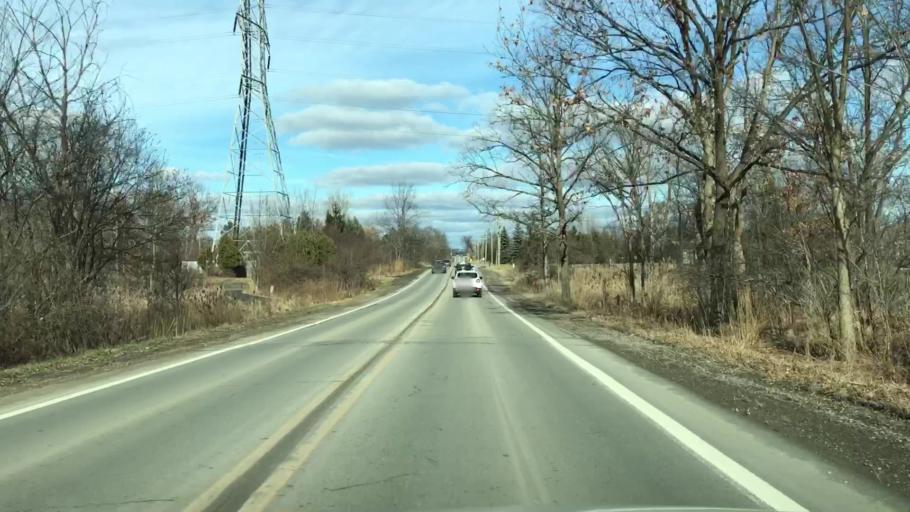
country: US
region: Michigan
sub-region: Oakland County
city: Auburn Hills
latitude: 42.7320
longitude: -83.1965
